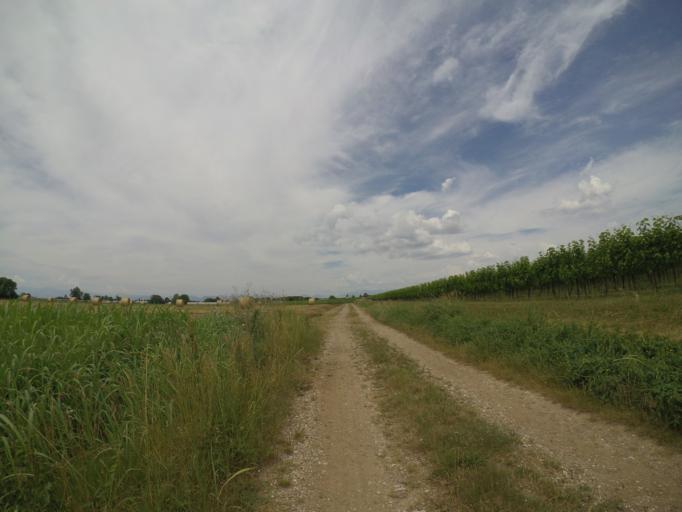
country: IT
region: Friuli Venezia Giulia
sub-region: Provincia di Udine
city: Bertiolo
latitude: 45.9340
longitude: 13.0455
